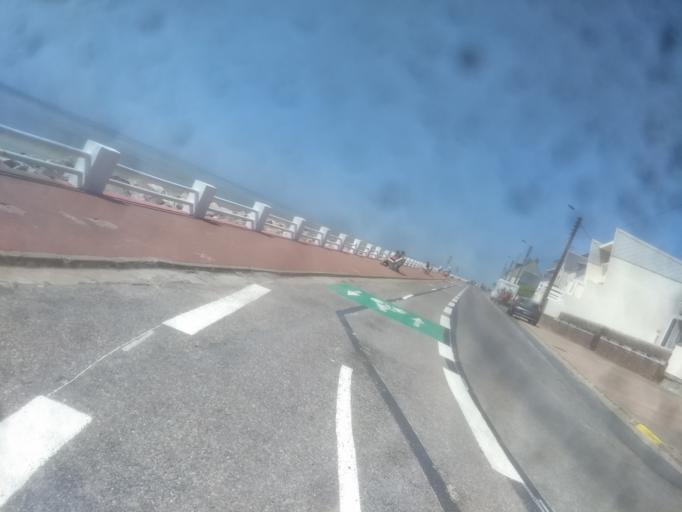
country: FR
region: Picardie
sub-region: Departement de la Somme
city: Le Crotoy
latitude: 50.2184
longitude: 1.6182
